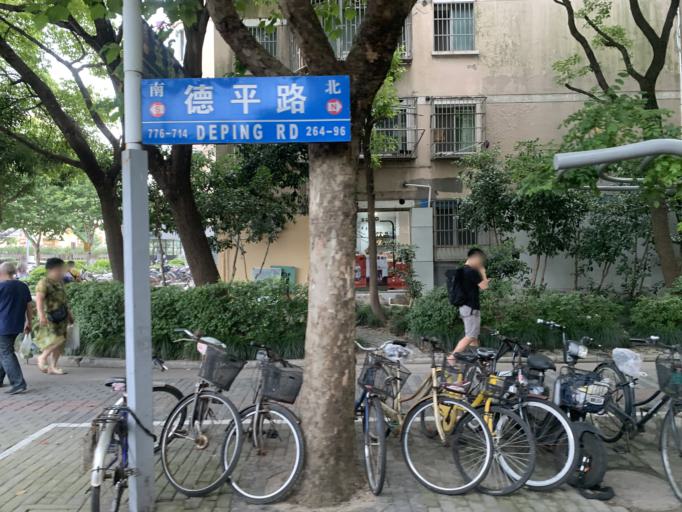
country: CN
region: Shanghai Shi
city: Pudong
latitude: 31.2483
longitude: 121.5604
